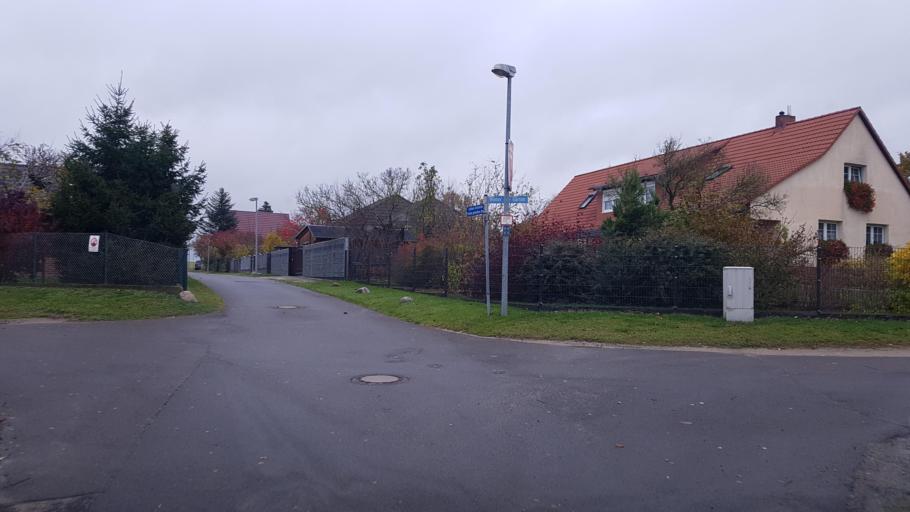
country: DE
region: Brandenburg
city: Drebkau
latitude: 51.6981
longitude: 14.2446
